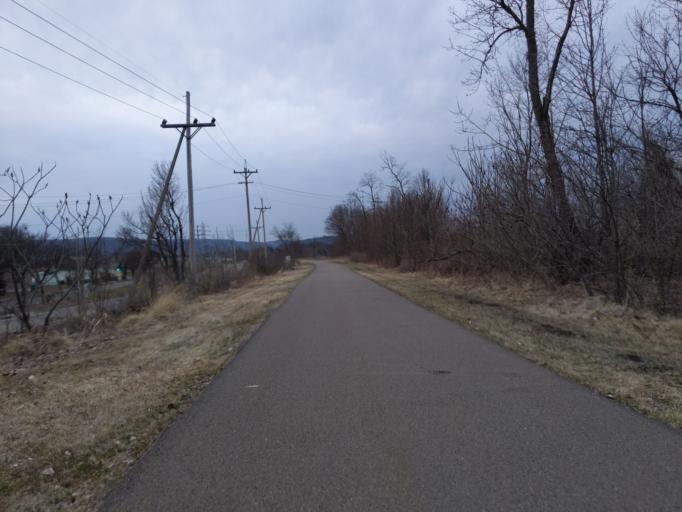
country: US
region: New York
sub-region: Chemung County
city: Elmira
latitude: 42.0975
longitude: -76.7949
